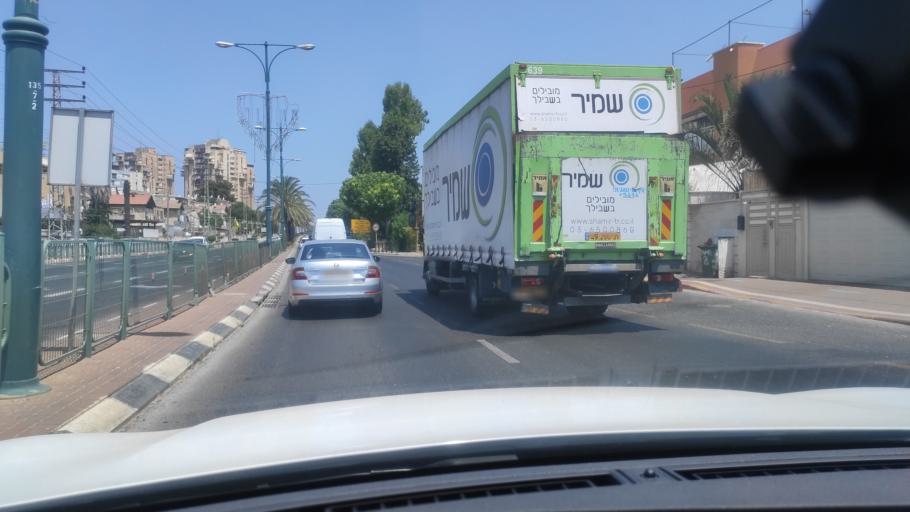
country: IL
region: Central District
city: Petah Tiqwa
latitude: 32.0972
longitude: 34.9014
